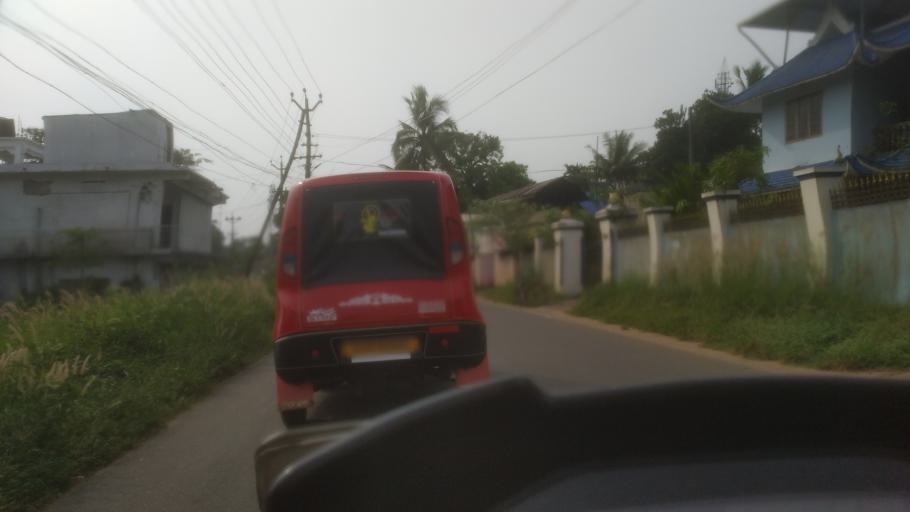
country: IN
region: Kerala
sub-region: Ernakulam
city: Aluva
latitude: 10.1555
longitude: 76.2974
